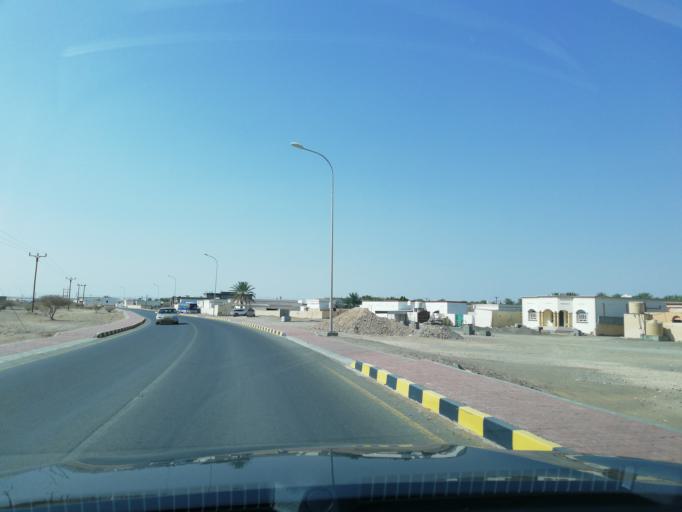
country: OM
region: Muhafazat ad Dakhiliyah
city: Adam
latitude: 22.3031
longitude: 58.0722
